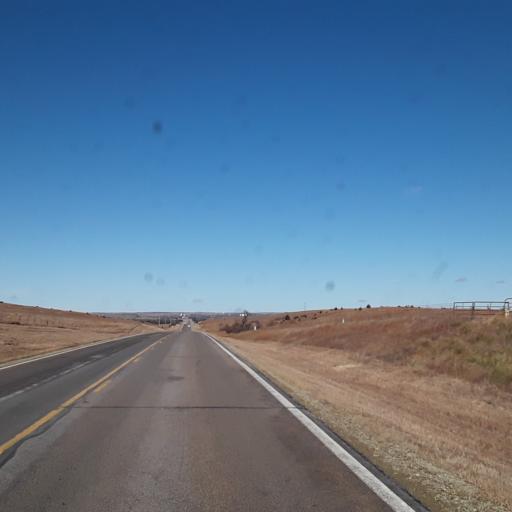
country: US
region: Kansas
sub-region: Lincoln County
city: Lincoln
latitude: 38.9526
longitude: -98.1511
